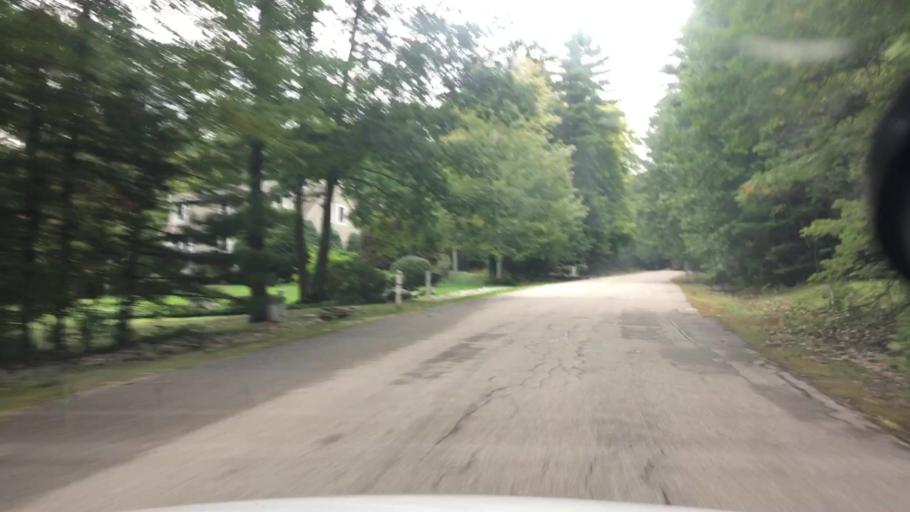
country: US
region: New Hampshire
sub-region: Strafford County
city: Rochester
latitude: 43.2802
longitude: -70.9569
